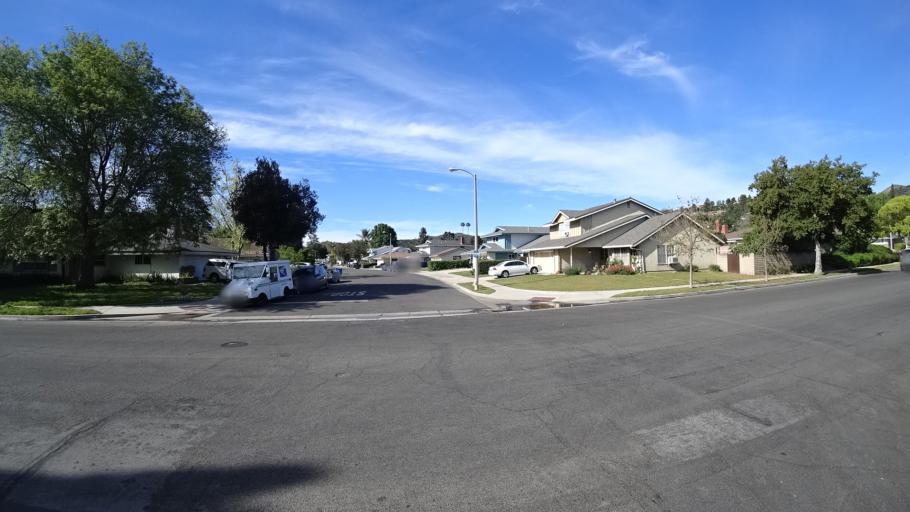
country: US
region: California
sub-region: Ventura County
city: Casa Conejo
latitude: 34.1758
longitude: -118.9551
